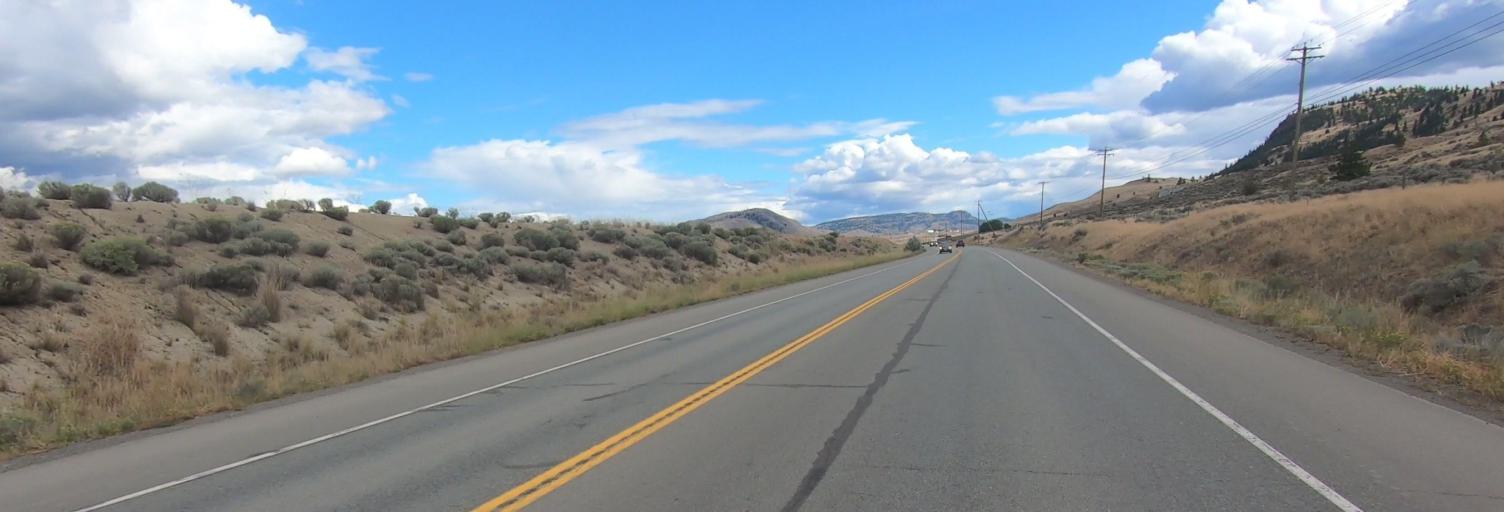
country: CA
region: British Columbia
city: Logan Lake
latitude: 50.7301
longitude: -120.6861
